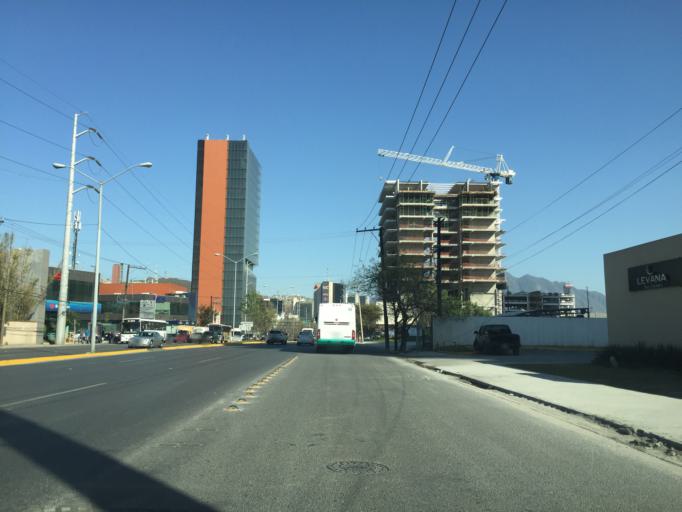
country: MX
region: Nuevo Leon
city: Garza Garcia
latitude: 25.6532
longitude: -100.3509
